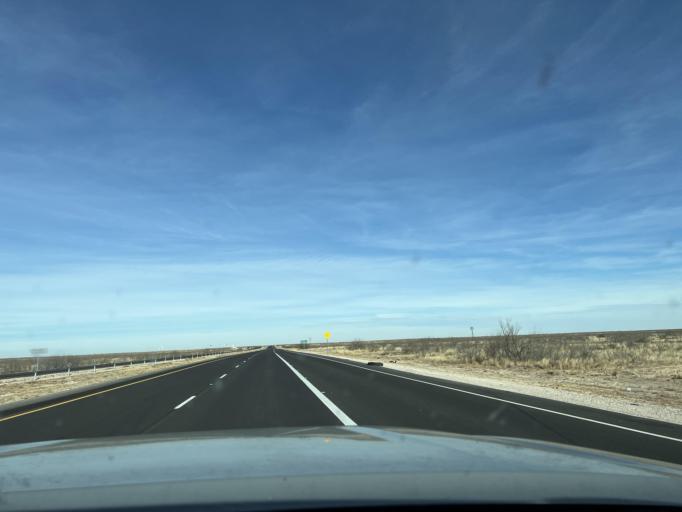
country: US
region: Texas
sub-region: Ector County
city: Gardendale
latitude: 32.0263
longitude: -102.4312
